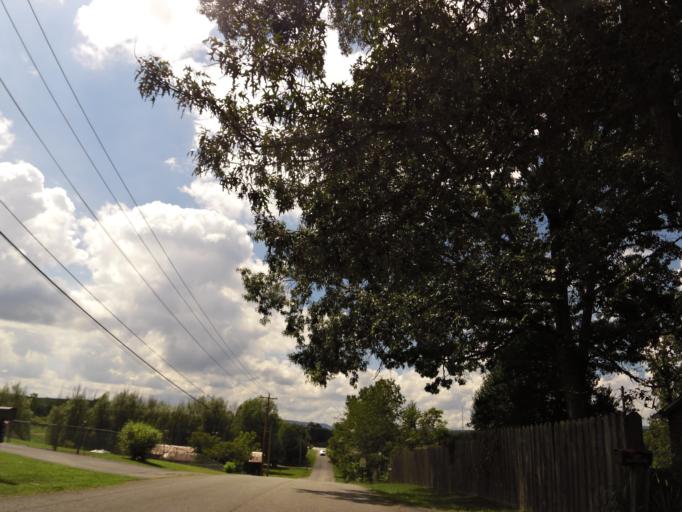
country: US
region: Tennessee
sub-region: Roane County
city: Rockwood
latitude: 35.8889
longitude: -84.7436
